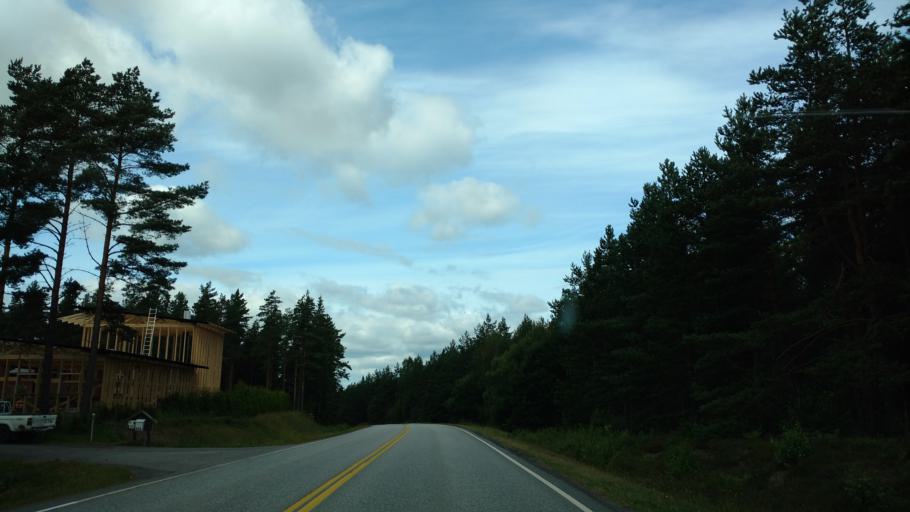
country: FI
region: Varsinais-Suomi
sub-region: Salo
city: Saerkisalo
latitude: 60.1685
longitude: 22.9835
